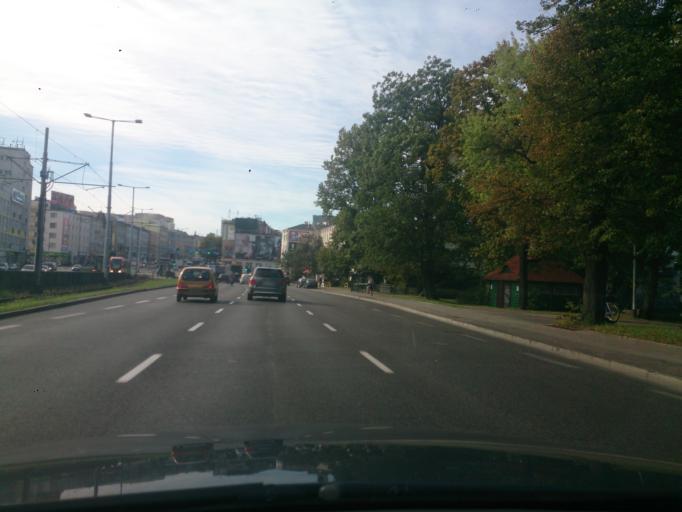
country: PL
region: Pomeranian Voivodeship
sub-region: Gdansk
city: Gdansk
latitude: 54.3755
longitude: 18.6172
